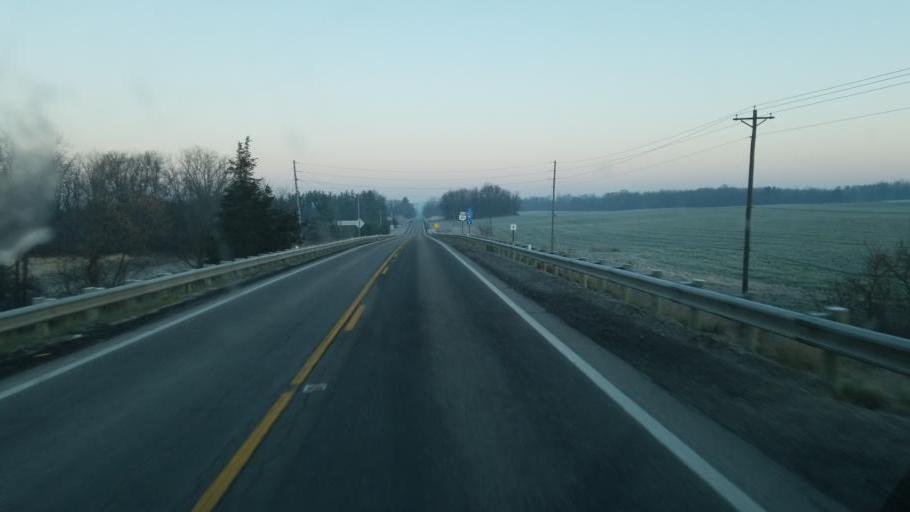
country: US
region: Ohio
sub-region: Wayne County
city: West Salem
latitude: 40.9362
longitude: -82.1093
